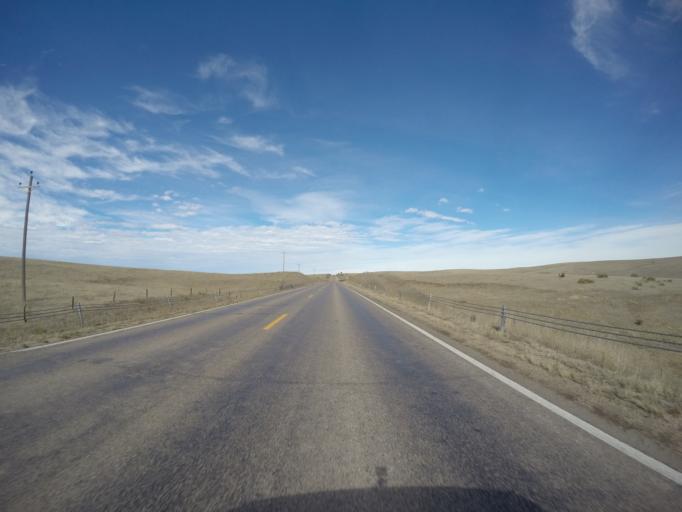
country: US
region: Nebraska
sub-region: Franklin County
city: Franklin
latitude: 40.1474
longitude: -98.9524
